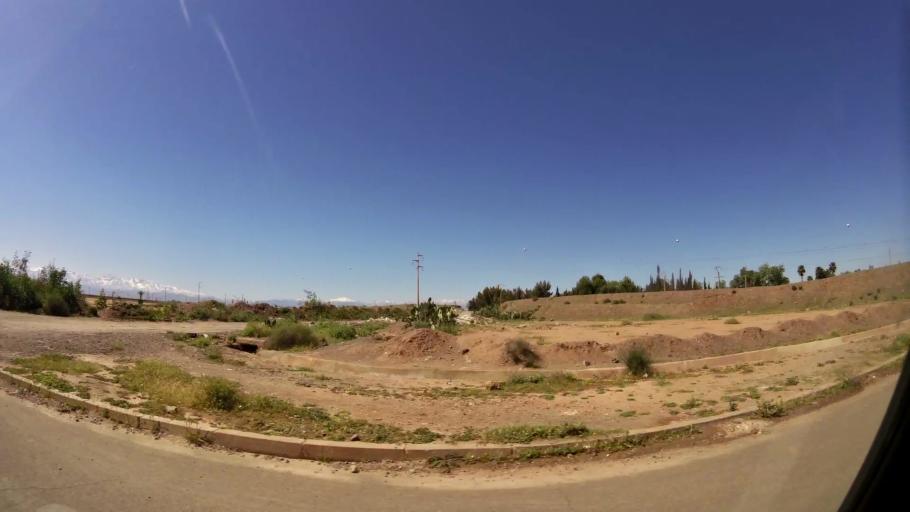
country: MA
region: Marrakech-Tensift-Al Haouz
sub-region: Marrakech
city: Marrakesh
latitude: 31.5719
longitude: -8.0632
